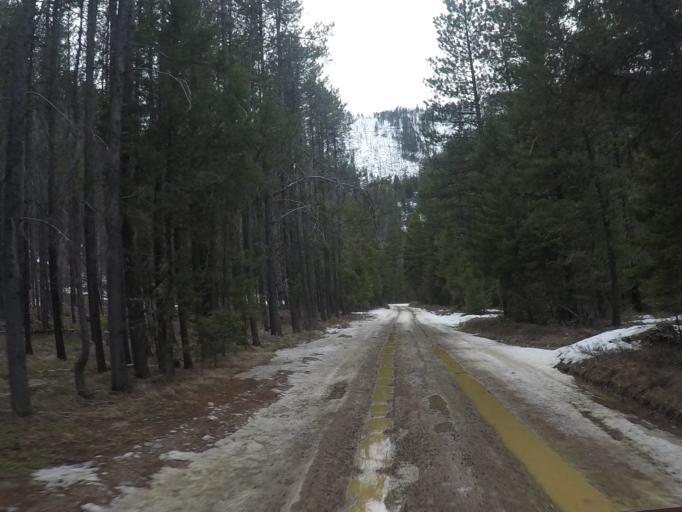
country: US
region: Montana
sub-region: Missoula County
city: Clinton
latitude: 46.5687
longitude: -113.6953
